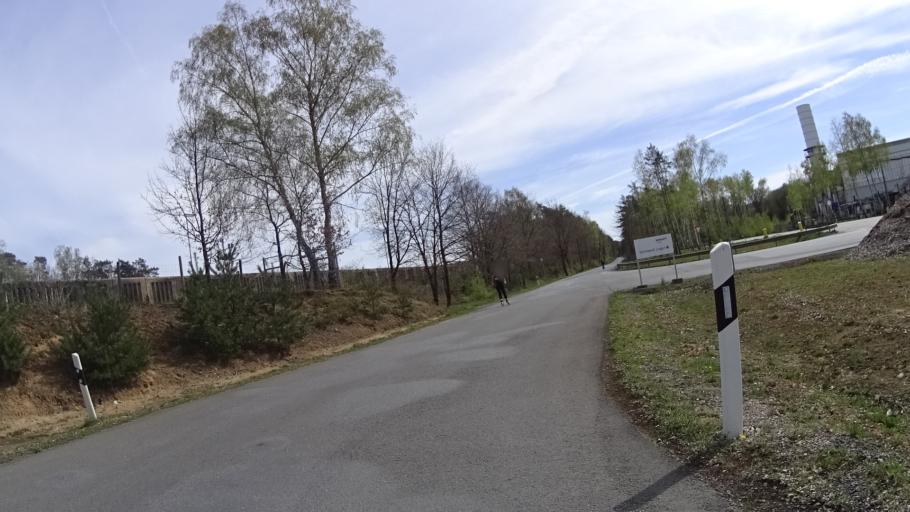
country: DE
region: Lower Saxony
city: Lingen
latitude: 52.4700
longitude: 7.3176
